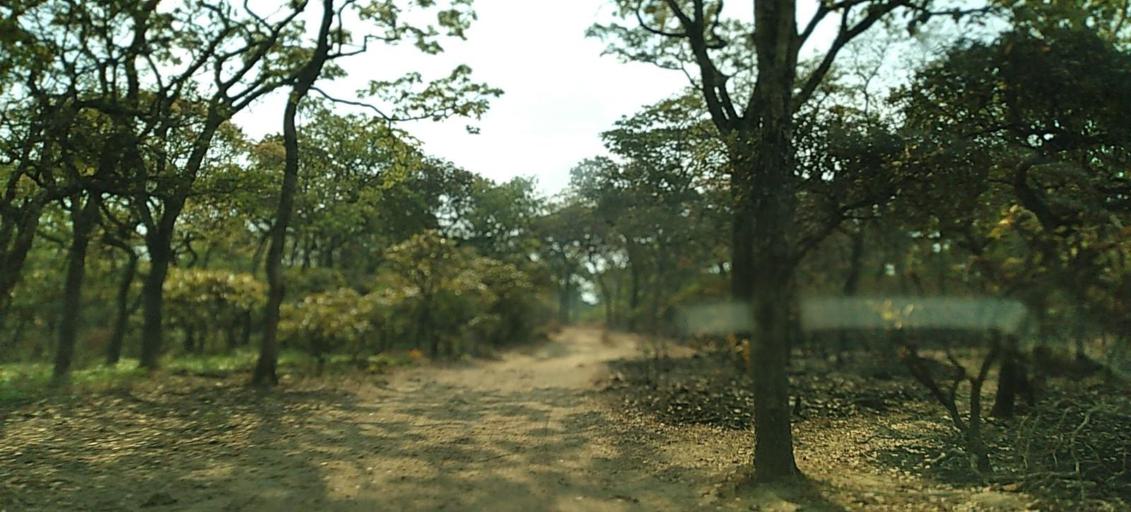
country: ZM
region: North-Western
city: Solwezi
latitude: -12.0728
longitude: 26.2313
